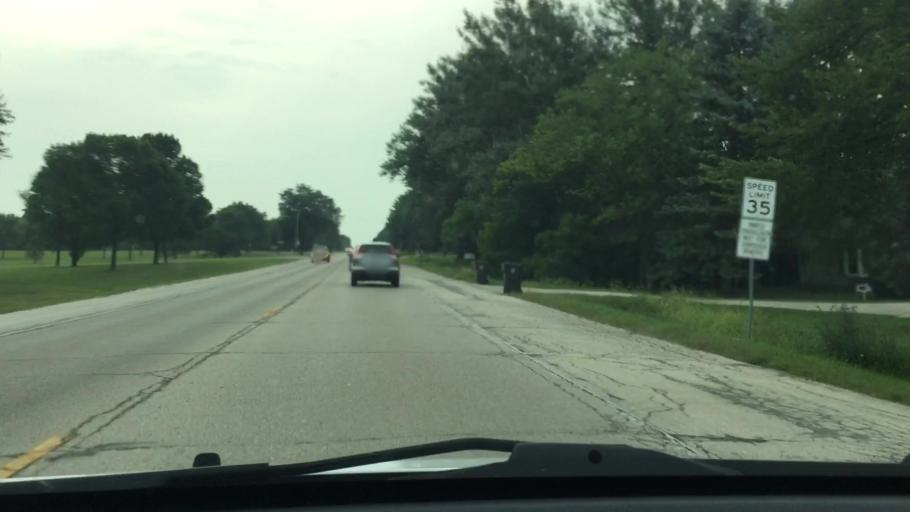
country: US
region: Wisconsin
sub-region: Waukesha County
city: New Berlin
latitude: 42.9955
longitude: -88.1013
